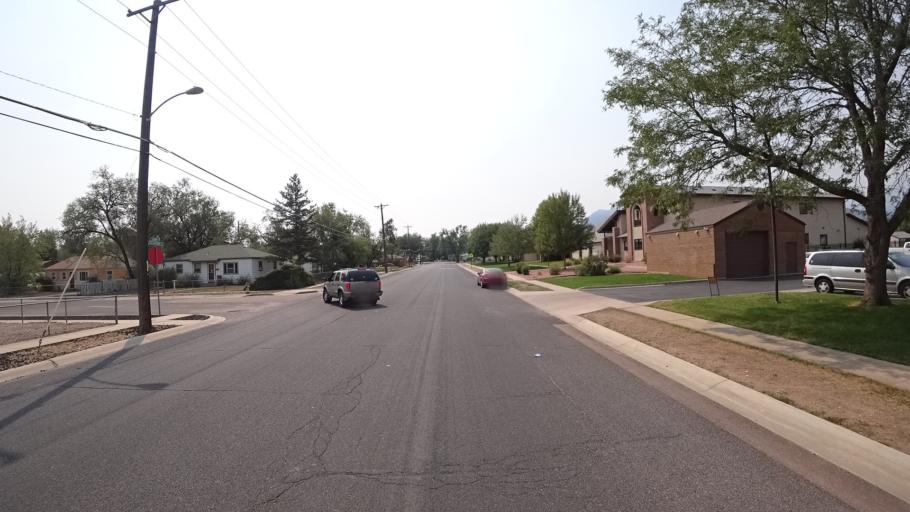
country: US
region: Colorado
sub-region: El Paso County
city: Colorado Springs
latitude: 38.8081
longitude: -104.8177
